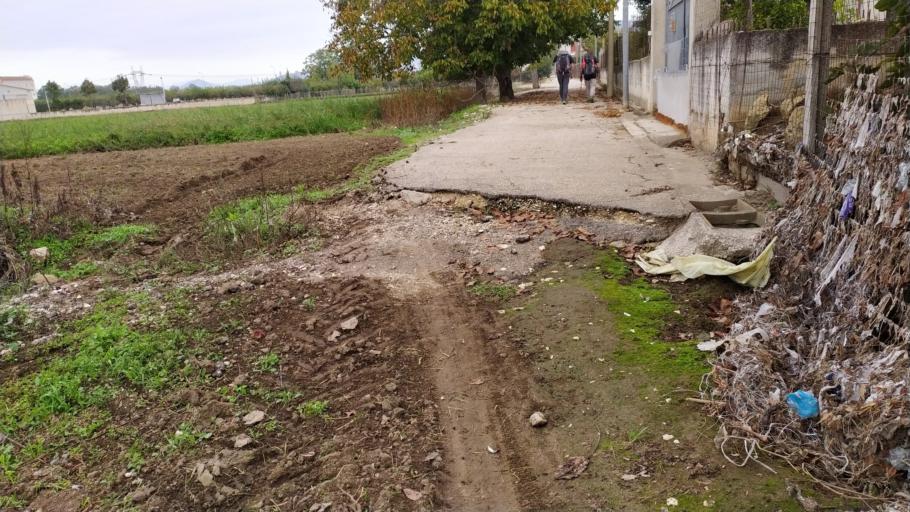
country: IT
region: Campania
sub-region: Provincia di Caserta
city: Montedecoro
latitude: 41.0020
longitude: 14.4139
